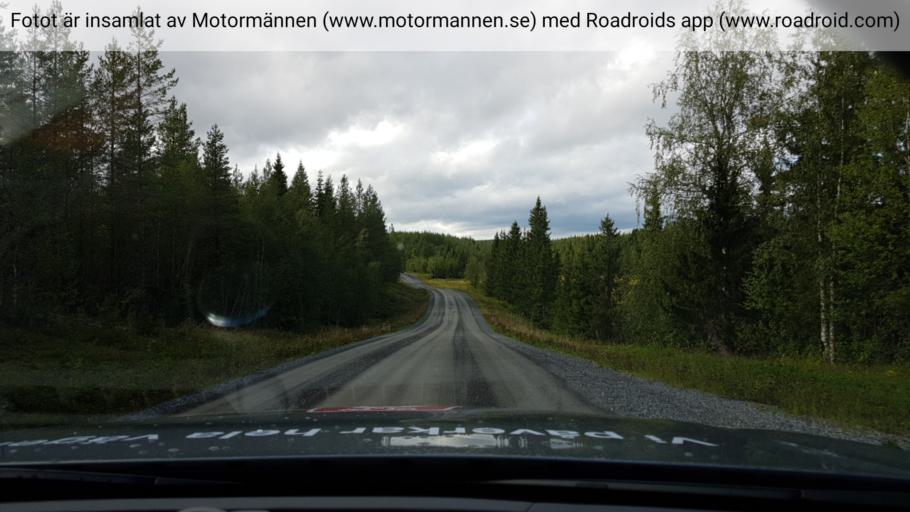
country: SE
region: Jaemtland
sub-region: Krokoms Kommun
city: Krokom
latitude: 63.7362
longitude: 14.4901
